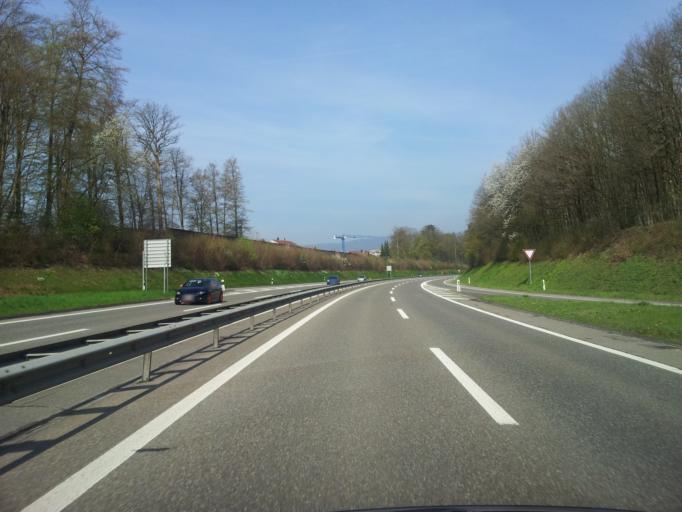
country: CH
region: Aargau
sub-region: Bezirk Aarau
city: Buchs
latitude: 47.3889
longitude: 8.0910
